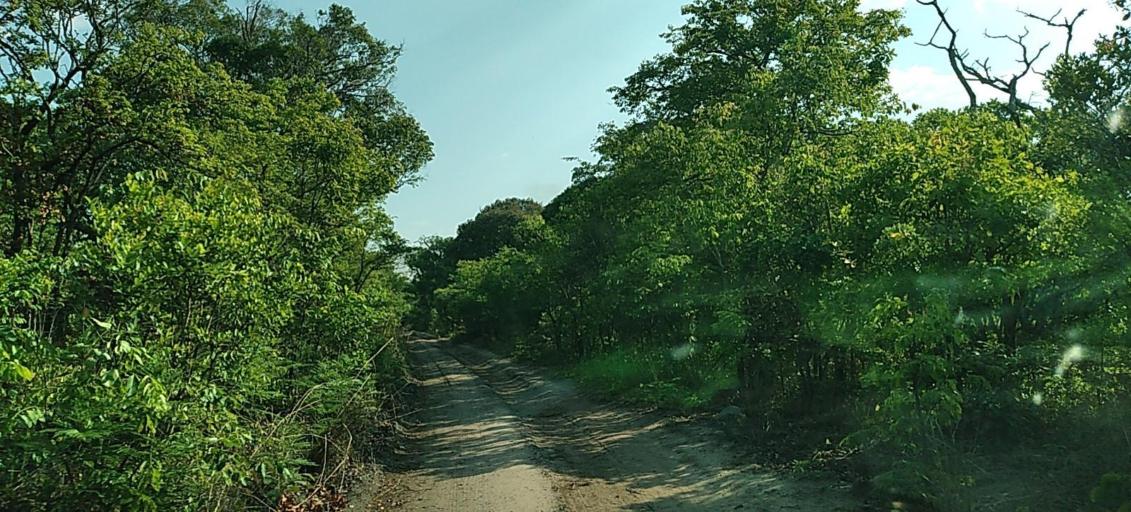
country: ZM
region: North-Western
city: Mwinilunga
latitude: -11.3179
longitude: 24.7399
